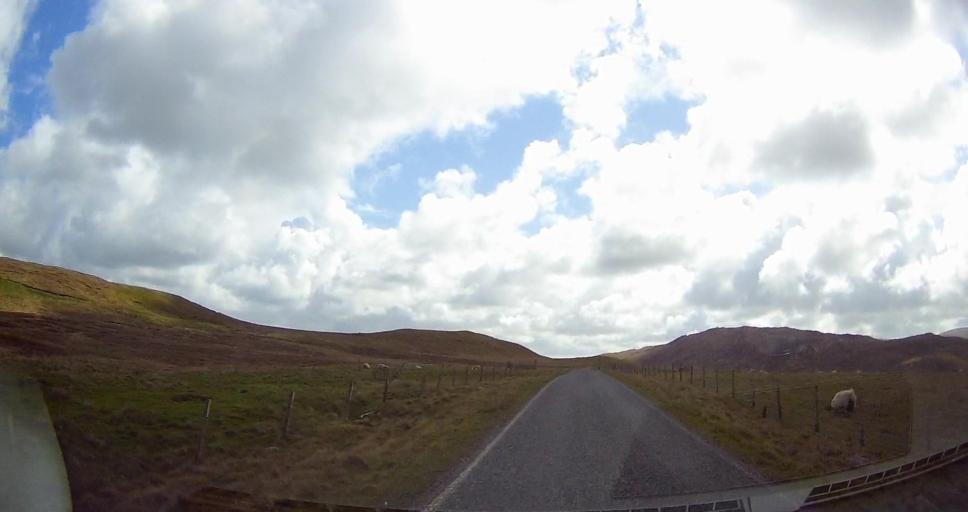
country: GB
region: Scotland
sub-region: Shetland Islands
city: Lerwick
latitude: 60.5613
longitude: -1.3341
